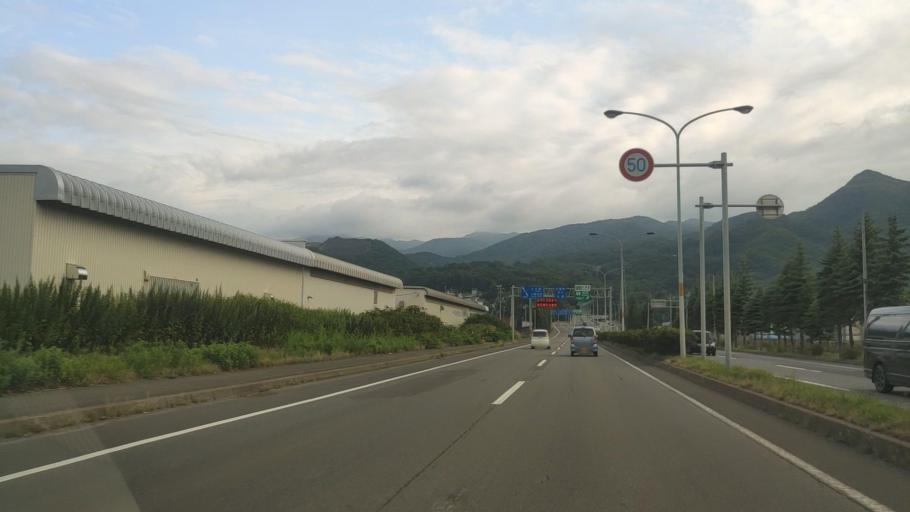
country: JP
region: Hokkaido
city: Otaru
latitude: 43.1404
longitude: 141.1789
